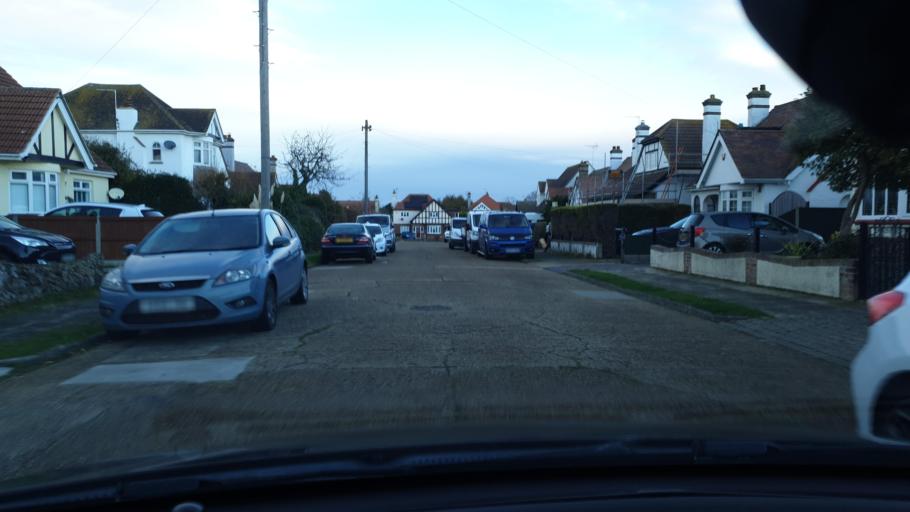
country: GB
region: England
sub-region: Essex
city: Clacton-on-Sea
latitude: 51.8008
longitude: 1.1689
